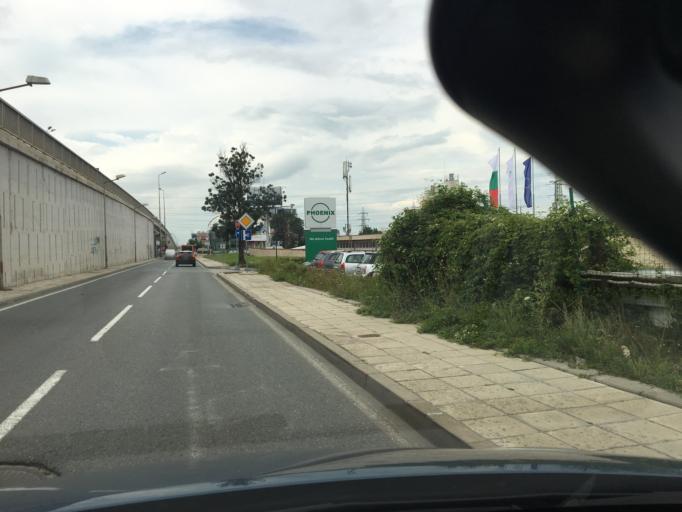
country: BG
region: Sofia-Capital
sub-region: Stolichna Obshtina
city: Sofia
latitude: 42.6324
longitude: 23.3357
